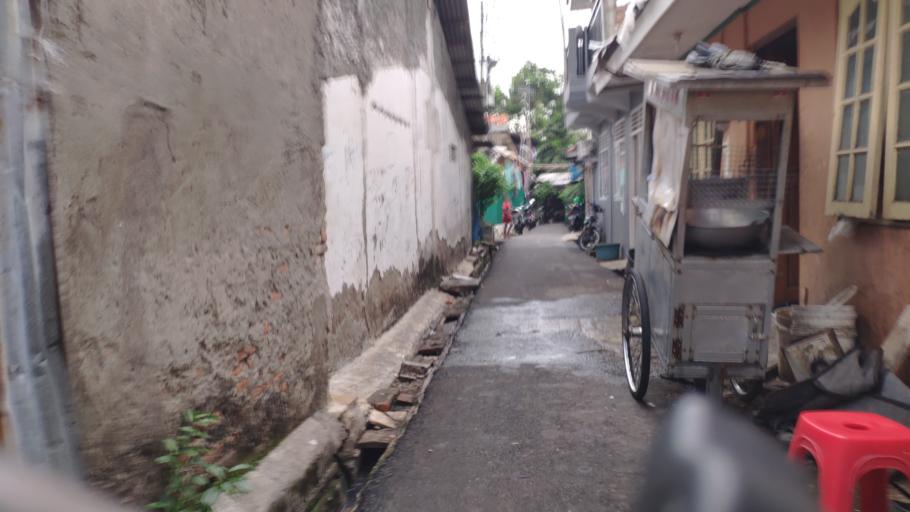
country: ID
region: Jakarta Raya
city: Jakarta
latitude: -6.2122
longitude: 106.8387
